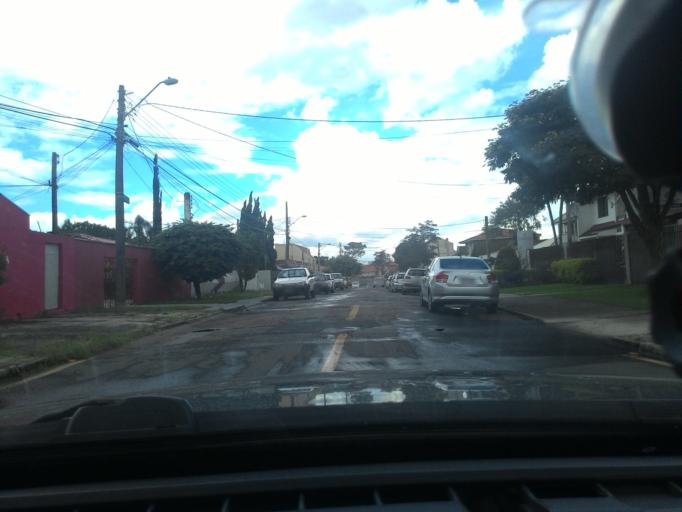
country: BR
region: Parana
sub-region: Pinhais
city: Pinhais
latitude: -25.4635
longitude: -49.2340
